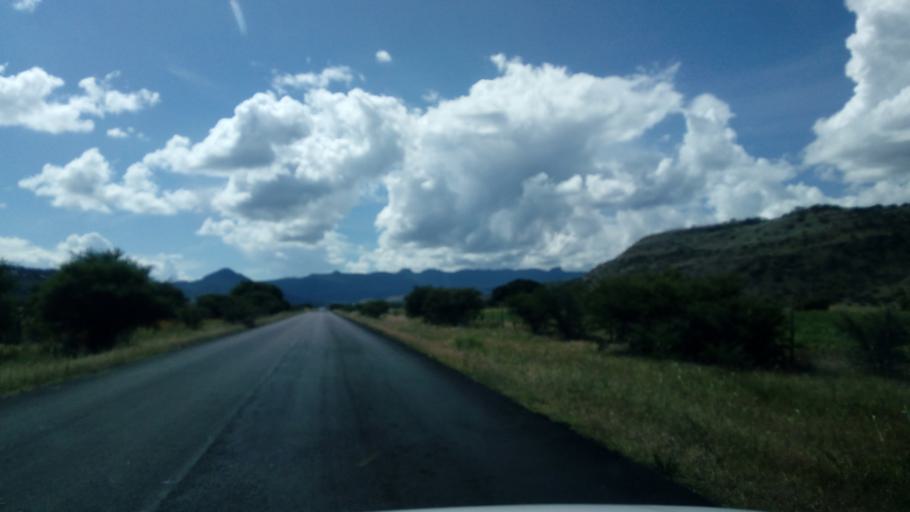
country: MX
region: Durango
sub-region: Durango
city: Jose Refugio Salcido
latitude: 23.8193
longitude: -104.4831
